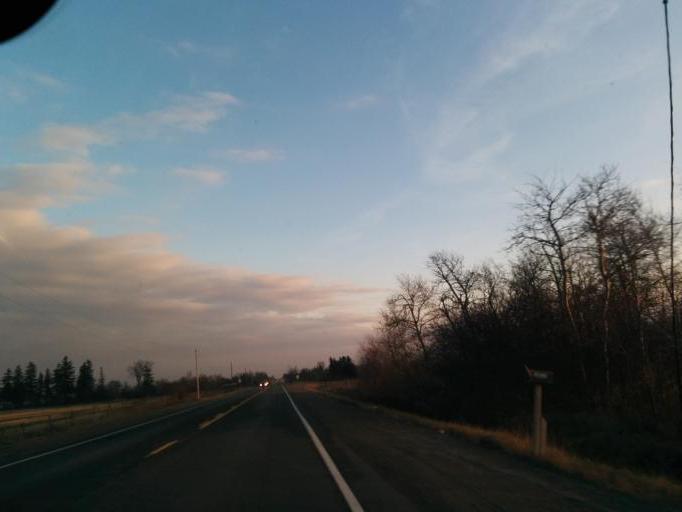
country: CA
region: Ontario
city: Brampton
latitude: 43.8558
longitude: -79.7766
